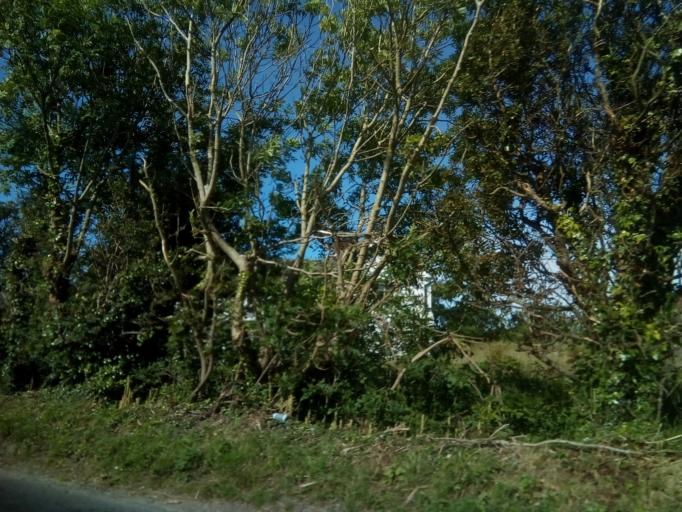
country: IE
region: Leinster
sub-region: Loch Garman
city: Loch Garman
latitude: 52.1890
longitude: -6.5617
